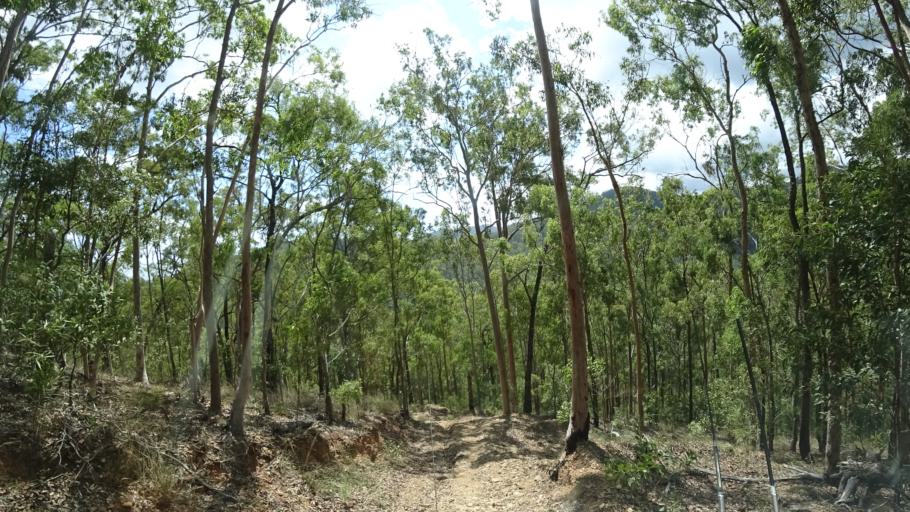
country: AU
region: Queensland
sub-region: Moreton Bay
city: Highvale
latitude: -27.3740
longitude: 152.7372
